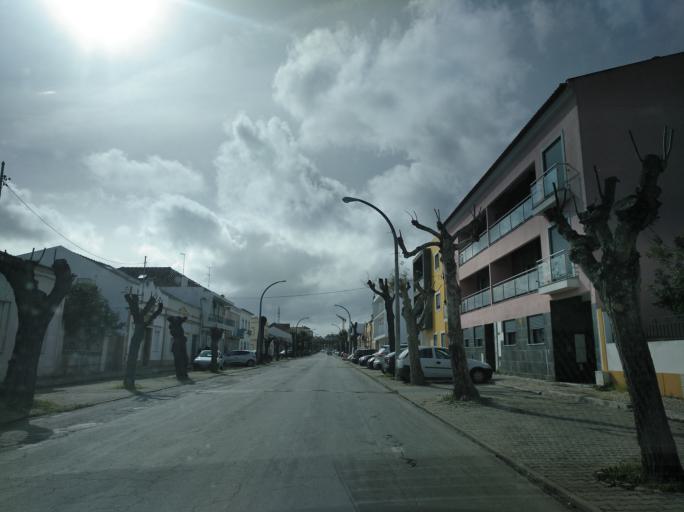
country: PT
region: Setubal
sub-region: Grandola
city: Grandola
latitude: 38.1782
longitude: -8.5628
